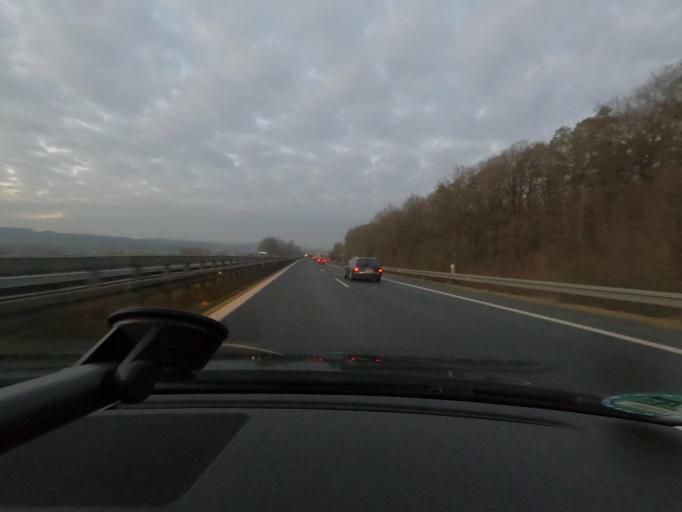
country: DE
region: Bavaria
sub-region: Upper Franconia
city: Ebensfeld
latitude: 50.0417
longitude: 10.9586
